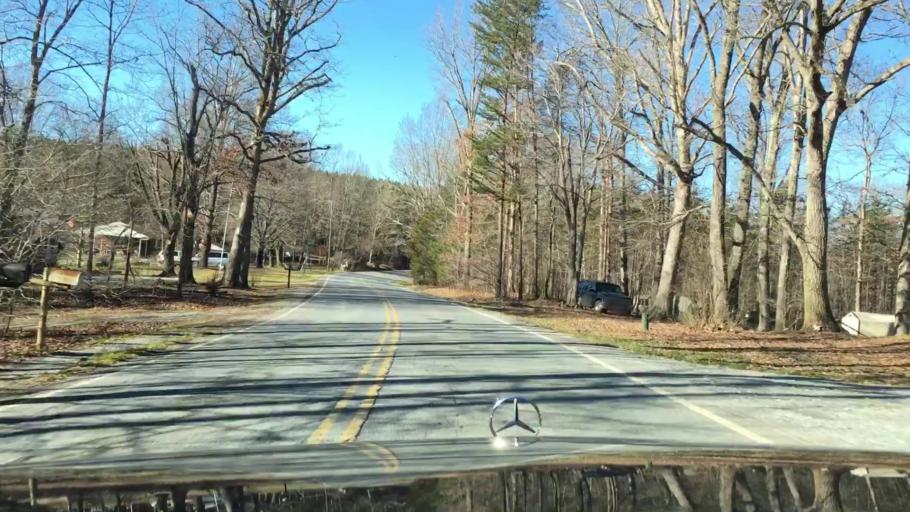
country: US
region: Virginia
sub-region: Pittsylvania County
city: Motley
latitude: 37.1583
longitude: -79.3961
